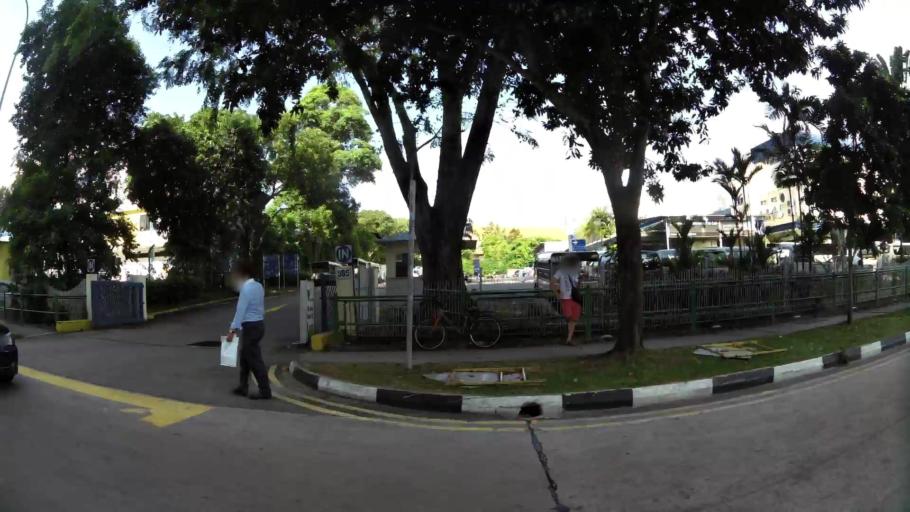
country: SG
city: Singapore
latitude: 1.3602
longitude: 103.8380
